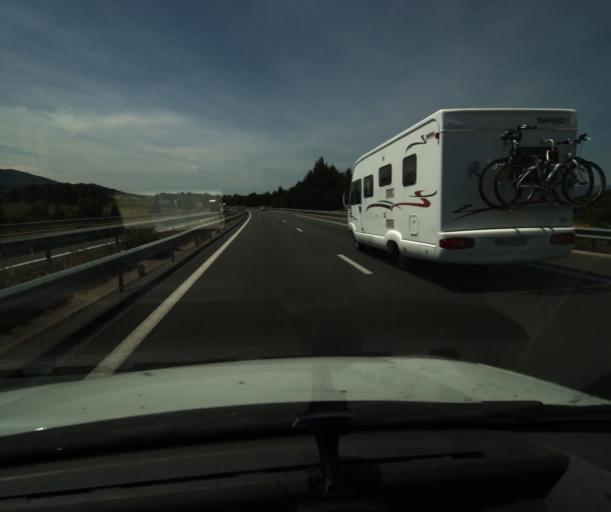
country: FR
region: Languedoc-Roussillon
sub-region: Departement de l'Aude
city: Capendu
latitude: 43.1783
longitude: 2.5915
